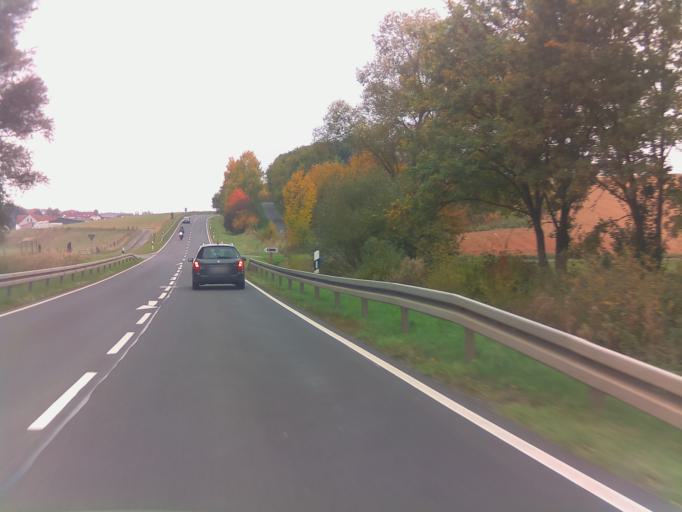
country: DE
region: Hesse
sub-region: Regierungsbezirk Kassel
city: Flieden
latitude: 50.4294
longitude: 9.5833
